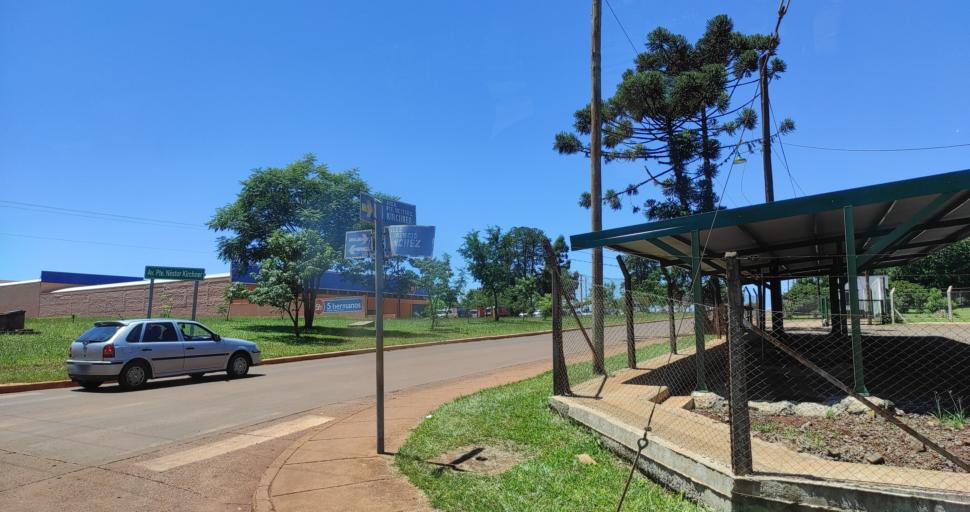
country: AR
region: Misiones
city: Dos de Mayo
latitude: -27.0052
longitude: -54.4771
